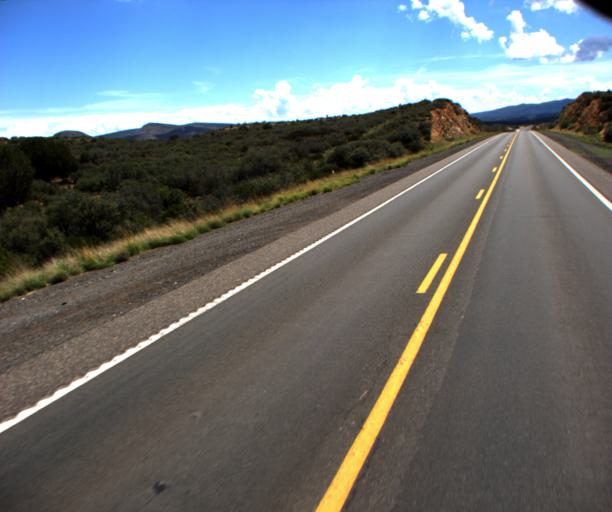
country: US
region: Arizona
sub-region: Yavapai County
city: Dewey-Humboldt
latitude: 34.5275
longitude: -112.0964
